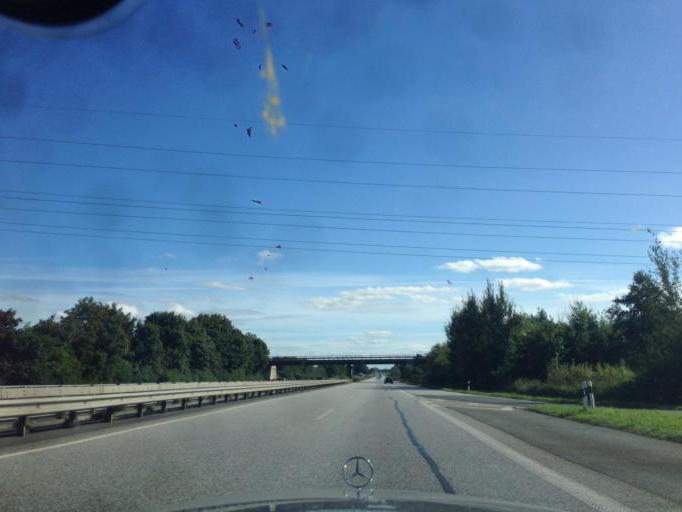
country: DE
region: Schleswig-Holstein
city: Jarplund-Weding
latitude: 54.7355
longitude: 9.3878
